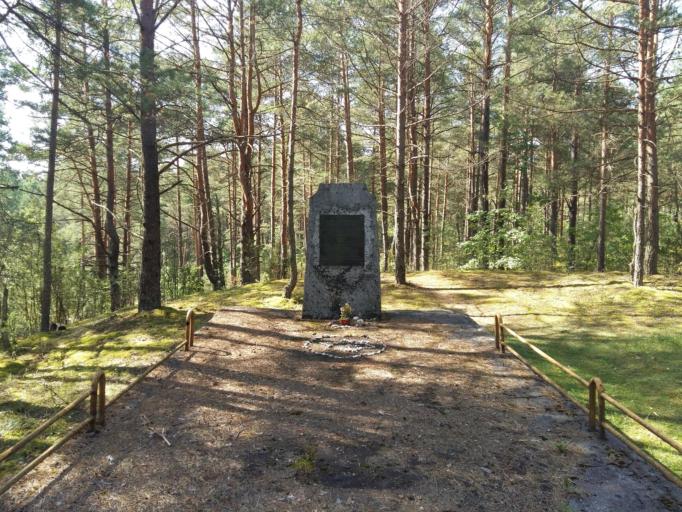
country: LT
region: Alytaus apskritis
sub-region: Alytaus rajonas
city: Daugai
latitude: 54.1579
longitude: 24.1925
